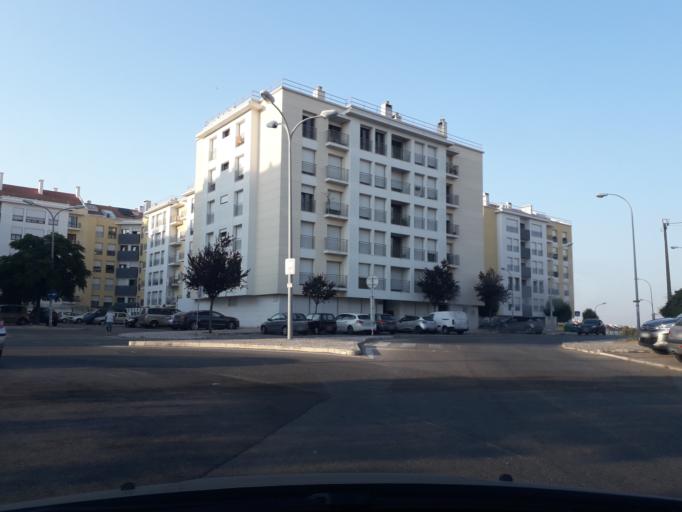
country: PT
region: Lisbon
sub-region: Amadora
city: Amadora
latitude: 38.7453
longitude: -9.2262
